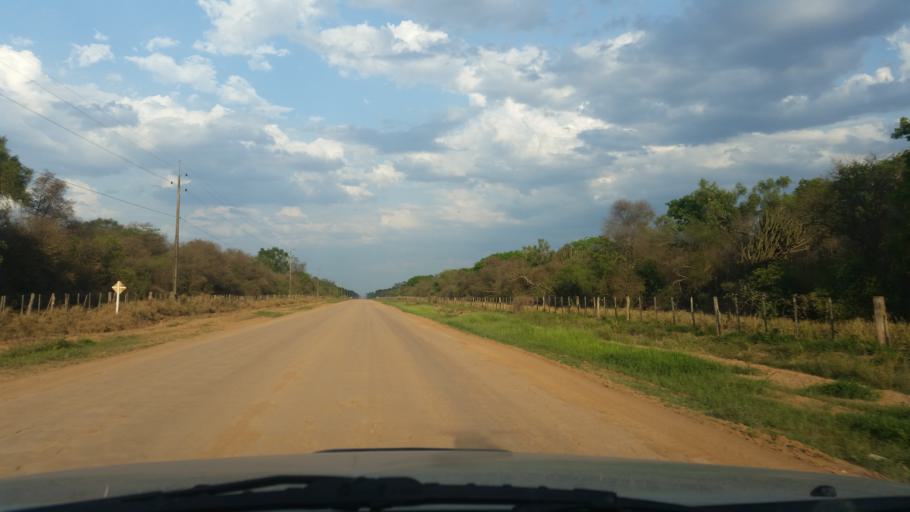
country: PY
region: Boqueron
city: Filadelfia
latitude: -22.3489
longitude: -59.9478
